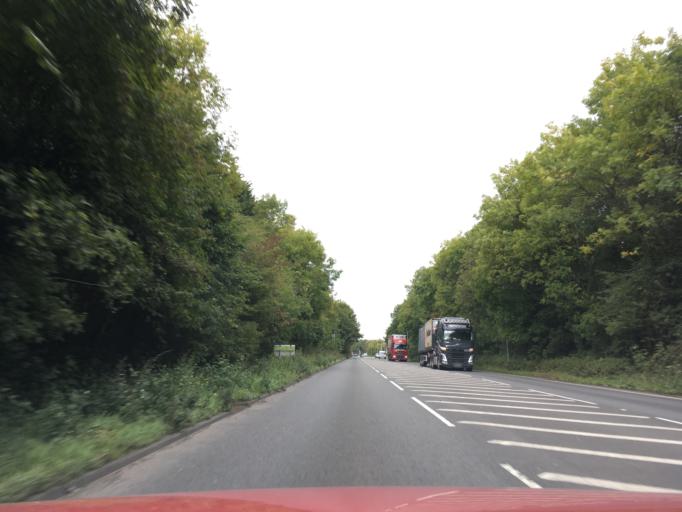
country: GB
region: Wales
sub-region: Monmouthshire
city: Magor
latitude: 51.5817
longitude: -2.8431
